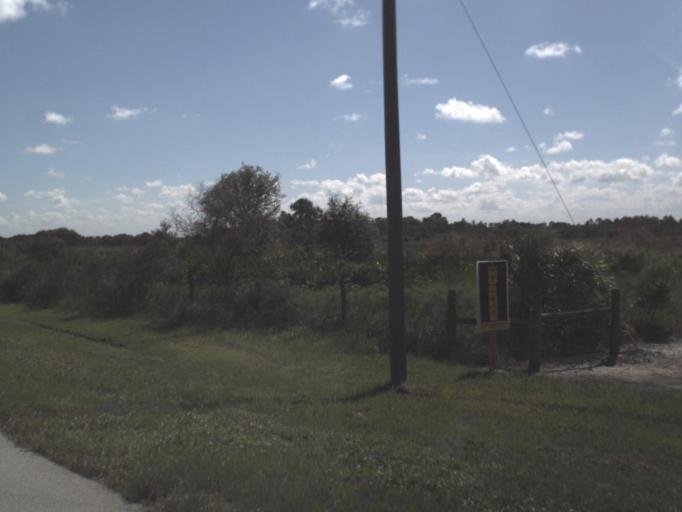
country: US
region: Florida
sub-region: Hendry County
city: Port LaBelle
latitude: 26.8121
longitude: -81.3920
